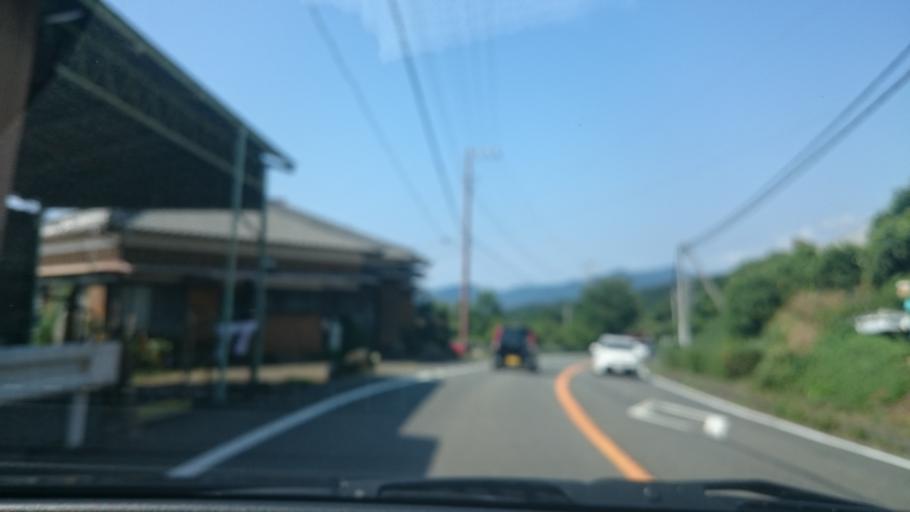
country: JP
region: Shizuoka
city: Heda
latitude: 34.8763
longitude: 138.7595
